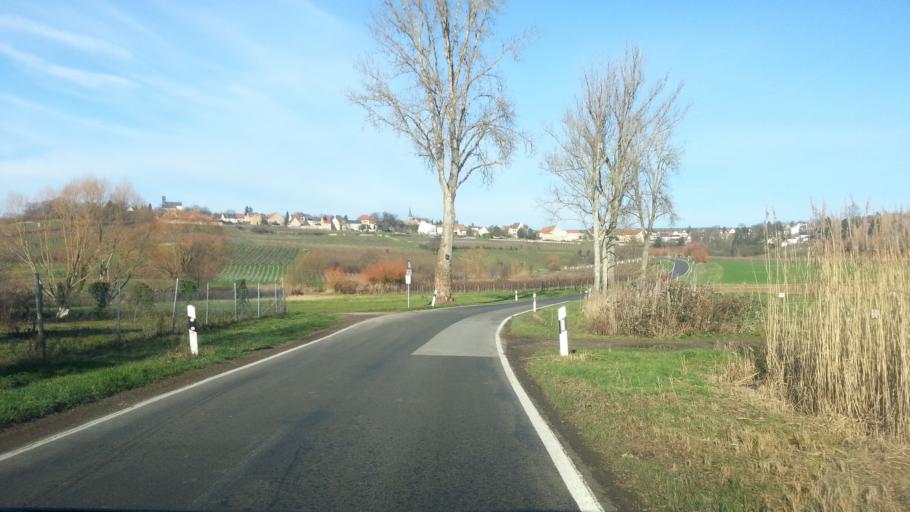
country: DE
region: Rheinland-Pfalz
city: Molsheim
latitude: 49.6397
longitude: 8.1699
